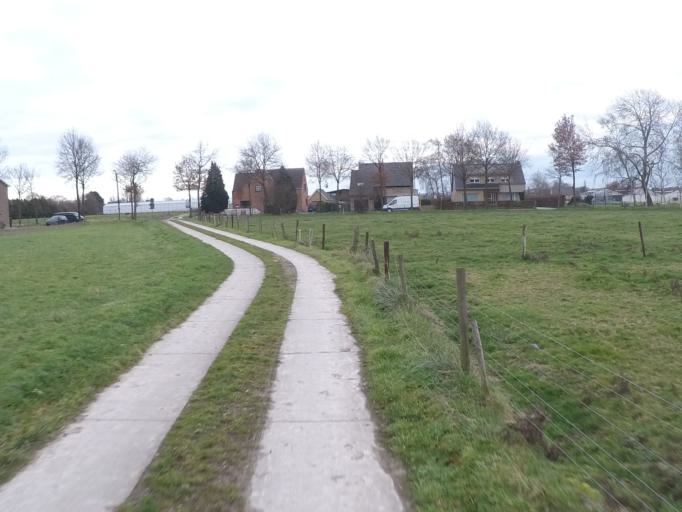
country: BE
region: Flanders
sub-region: Provincie Vlaams-Brabant
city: Merchtem
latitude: 50.9812
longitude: 4.2193
